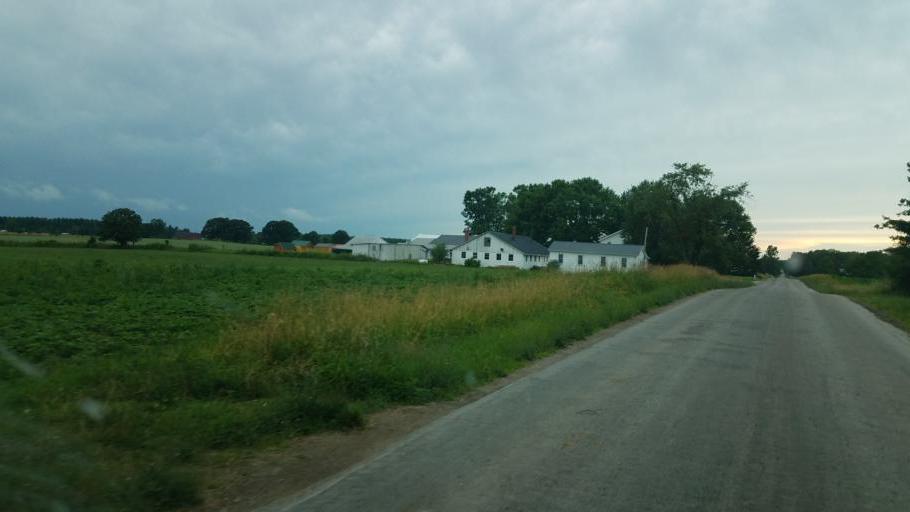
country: US
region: Ohio
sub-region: Huron County
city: Greenwich
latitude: 40.9315
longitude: -82.4371
